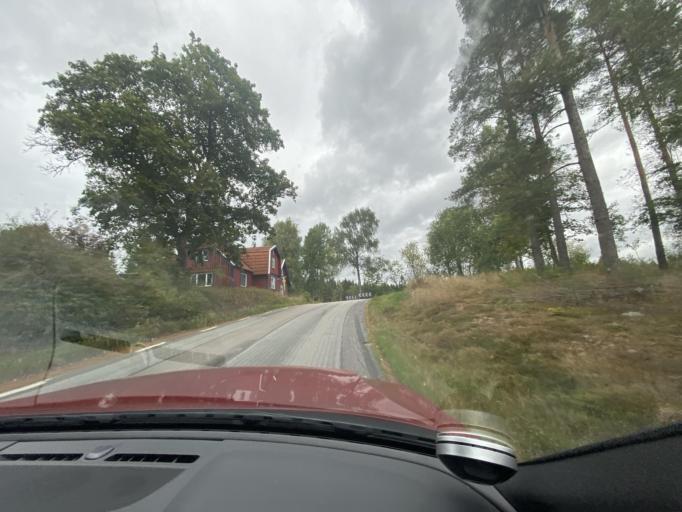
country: SE
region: Kronoberg
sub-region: Markaryds Kommun
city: Markaryd
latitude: 56.4874
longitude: 13.5908
